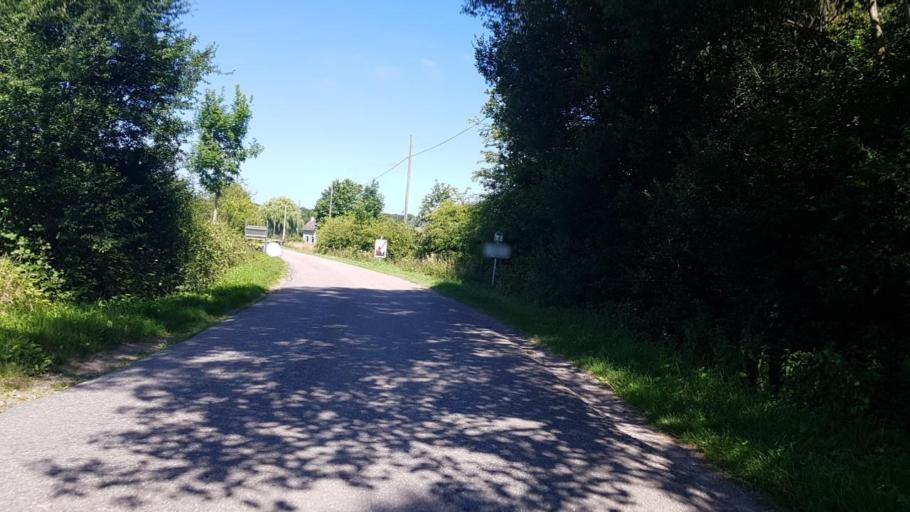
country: BE
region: Wallonia
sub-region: Province du Hainaut
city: Momignies
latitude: 50.0720
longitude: 4.2351
